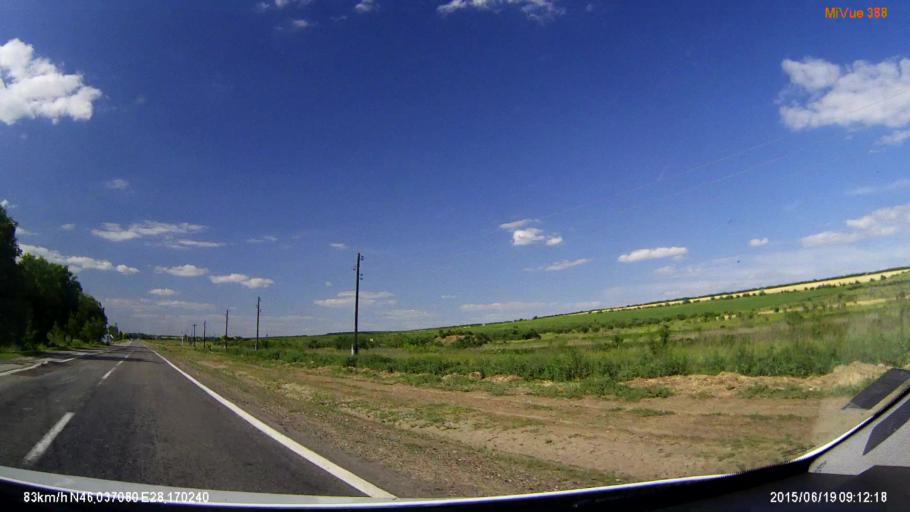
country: RO
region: Vaslui
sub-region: Oras Murgeni
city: Carja
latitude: 46.0369
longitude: 28.1700
